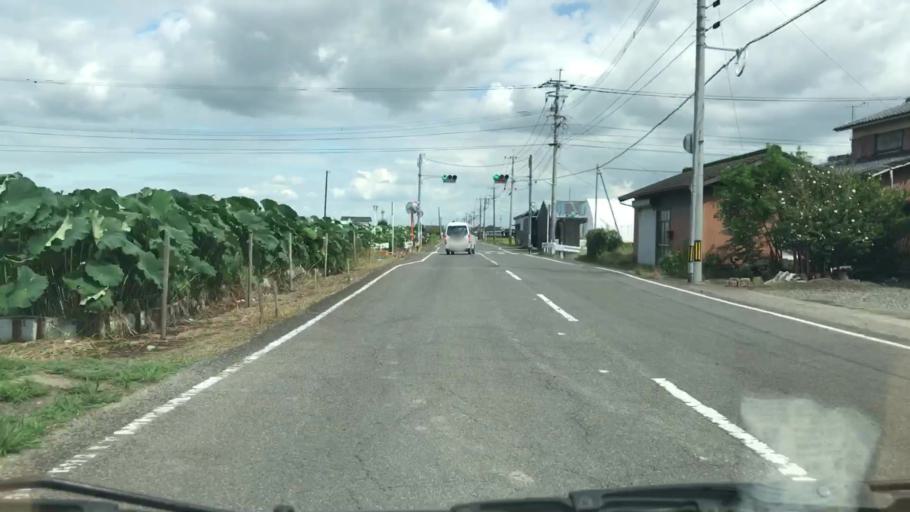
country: JP
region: Saga Prefecture
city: Saga-shi
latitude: 33.1956
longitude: 130.1866
